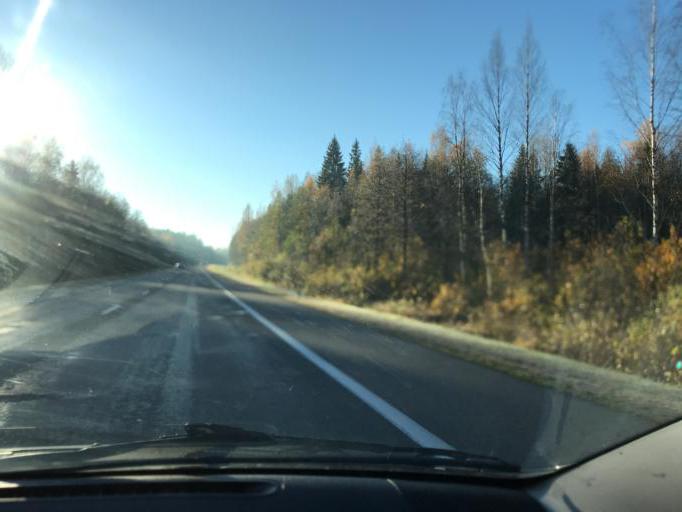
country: BY
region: Vitebsk
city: Vitebsk
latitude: 54.8936
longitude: 30.3819
